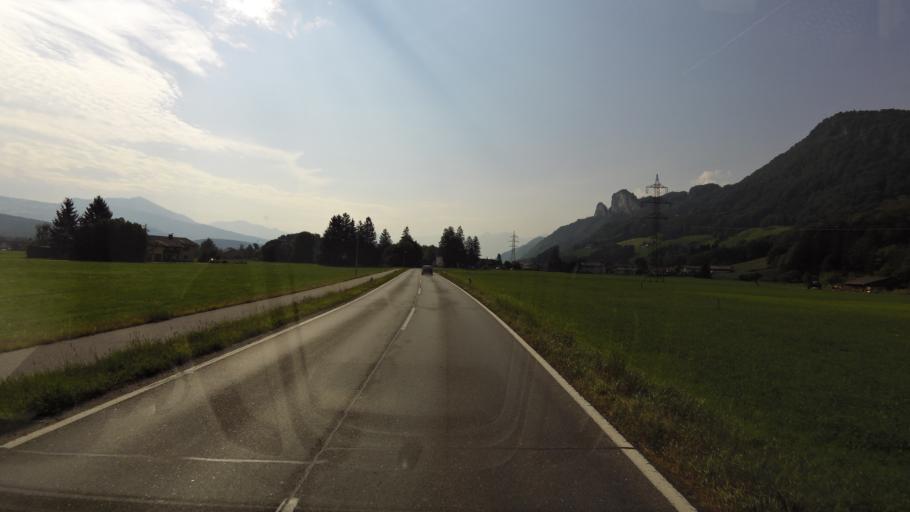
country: DE
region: Bavaria
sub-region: Upper Bavaria
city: Marktschellenberg
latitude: 47.7116
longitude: 13.0653
